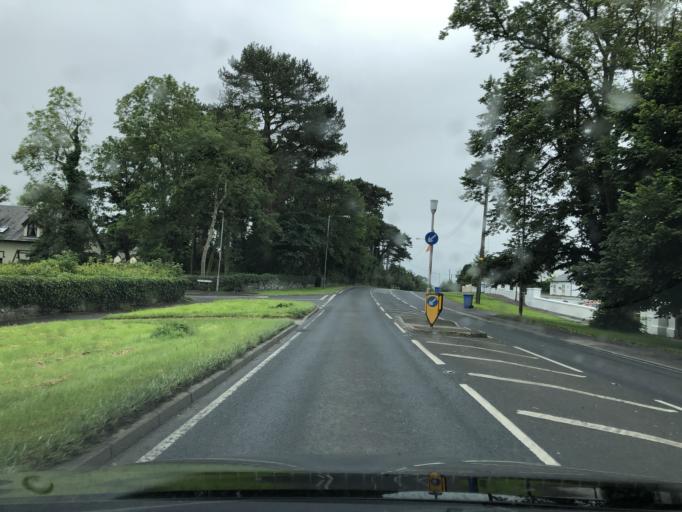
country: GB
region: Northern Ireland
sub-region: Down District
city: Dundrum
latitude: 54.3066
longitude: -5.8413
